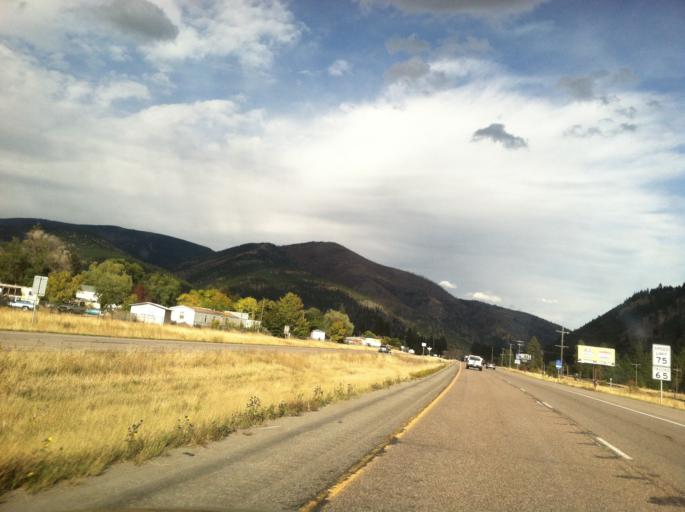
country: US
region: Montana
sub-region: Missoula County
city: East Missoula
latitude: 46.8682
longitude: -113.9446
